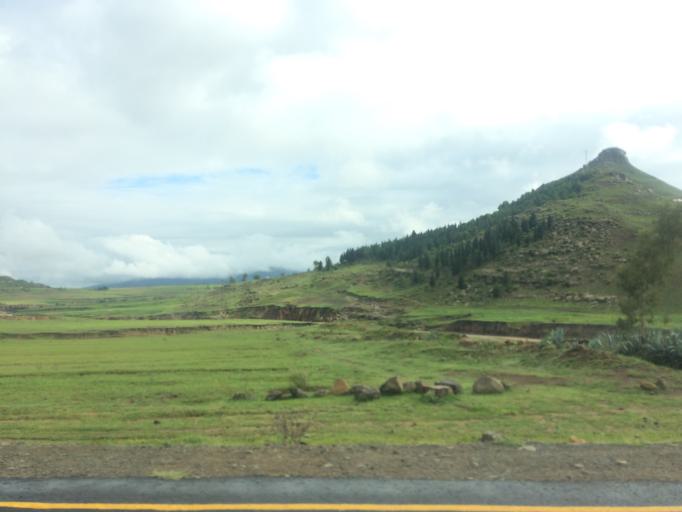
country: LS
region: Mafeteng
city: Mafeteng
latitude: -29.6978
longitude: 27.4571
